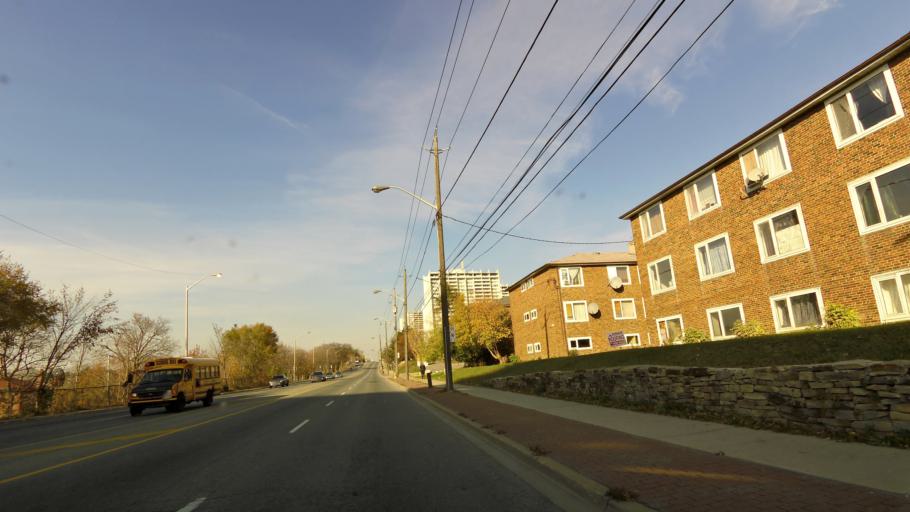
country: CA
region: Ontario
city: Concord
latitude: 43.7254
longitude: -79.5096
